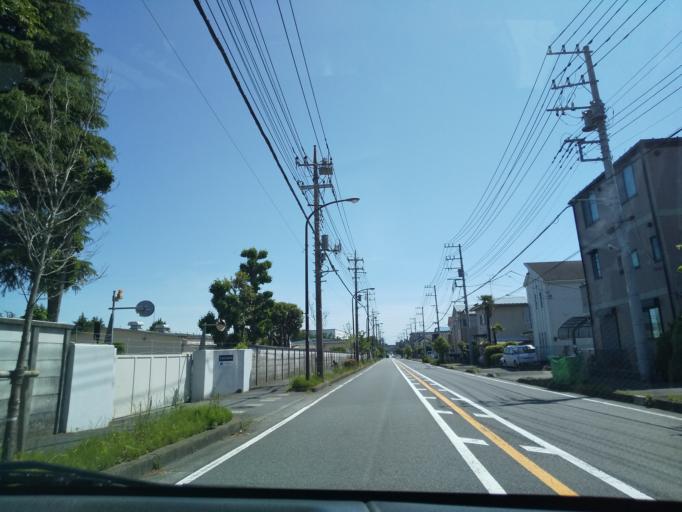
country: JP
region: Tokyo
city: Hachioji
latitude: 35.5938
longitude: 139.3578
